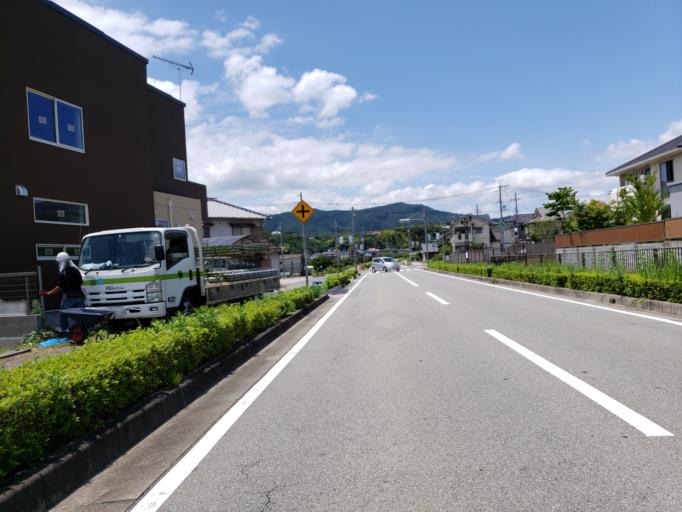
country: JP
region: Hyogo
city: Himeji
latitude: 34.9286
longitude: 134.7348
